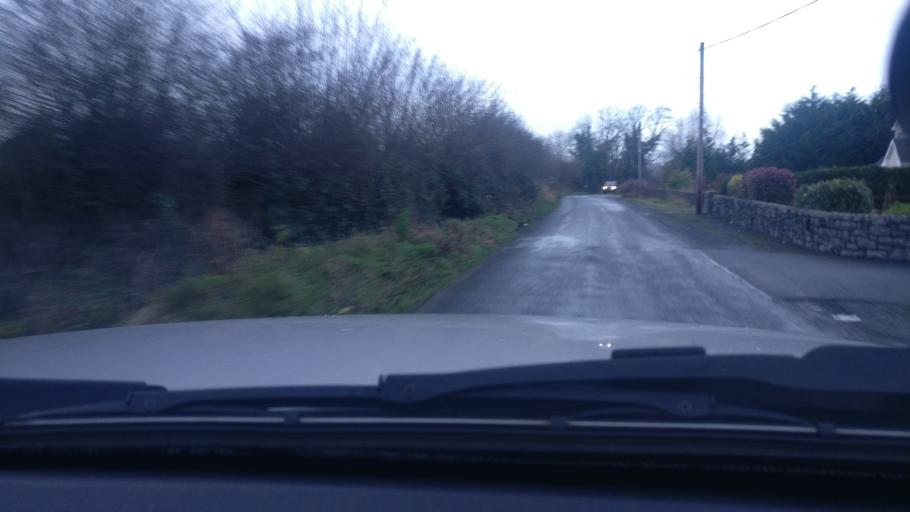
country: IE
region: Connaught
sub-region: County Galway
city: Loughrea
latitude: 53.1626
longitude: -8.5057
